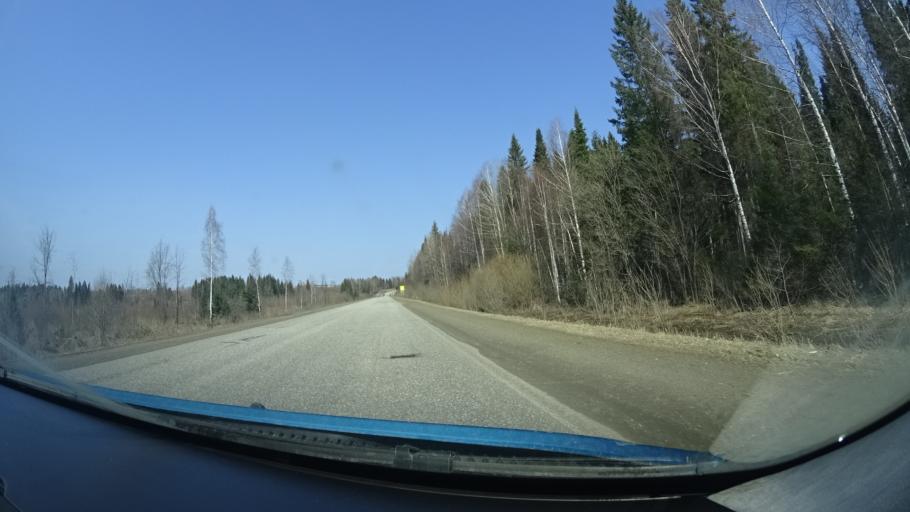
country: RU
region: Perm
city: Osa
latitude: 57.3839
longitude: 55.6090
